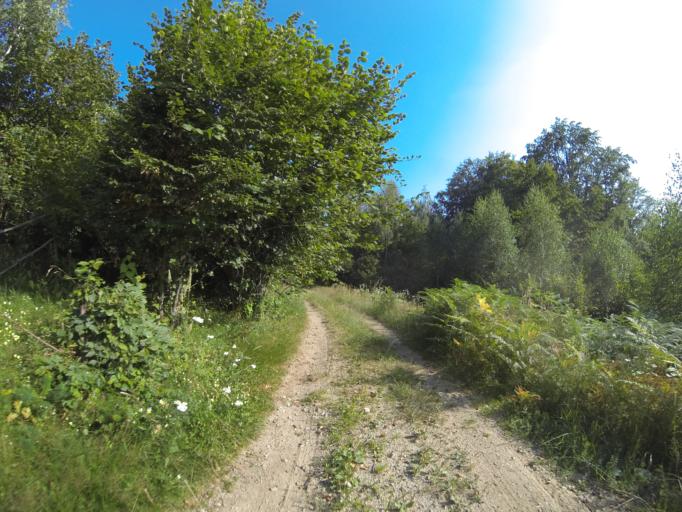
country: RO
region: Valcea
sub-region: Comuna Vaideeni
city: Vaideeni
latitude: 45.2085
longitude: 23.9716
